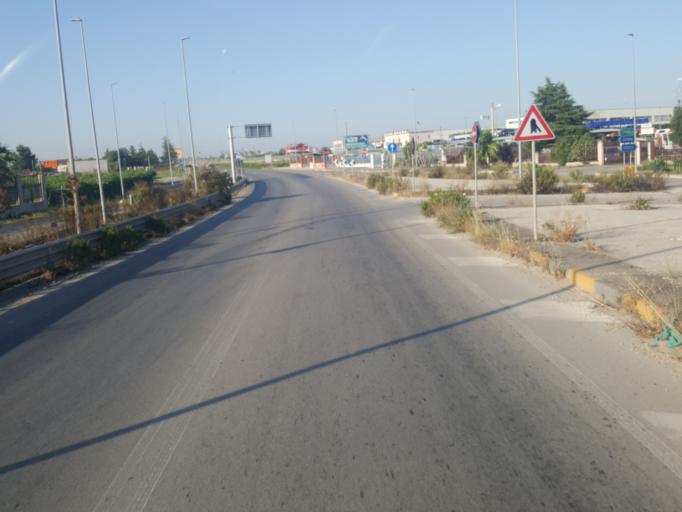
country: IT
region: Apulia
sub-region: Provincia di Foggia
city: Cerignola
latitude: 41.3121
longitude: 15.8997
